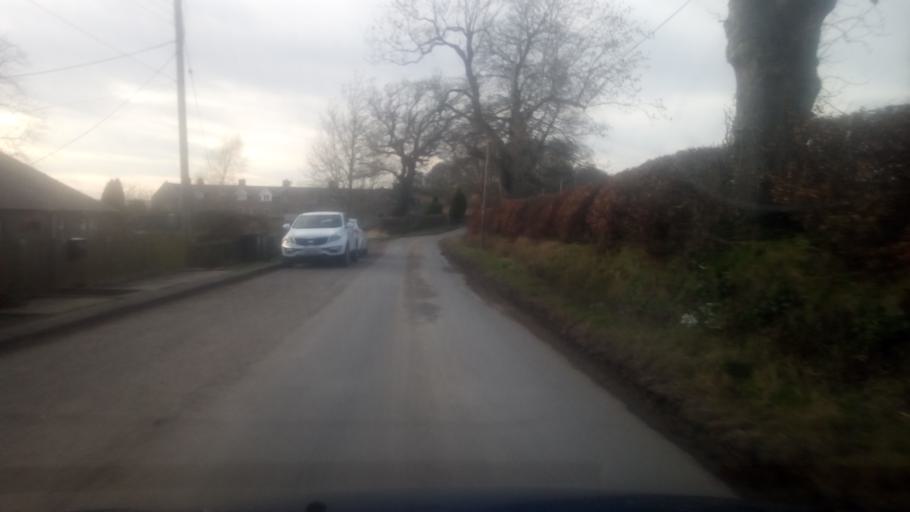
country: GB
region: Scotland
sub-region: The Scottish Borders
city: Jedburgh
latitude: 55.4091
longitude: -2.6080
